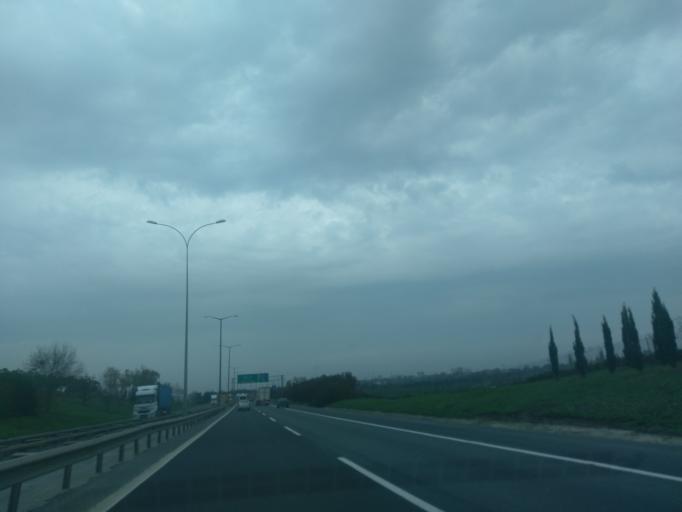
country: TR
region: Istanbul
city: Muratbey
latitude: 41.0825
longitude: 28.5080
